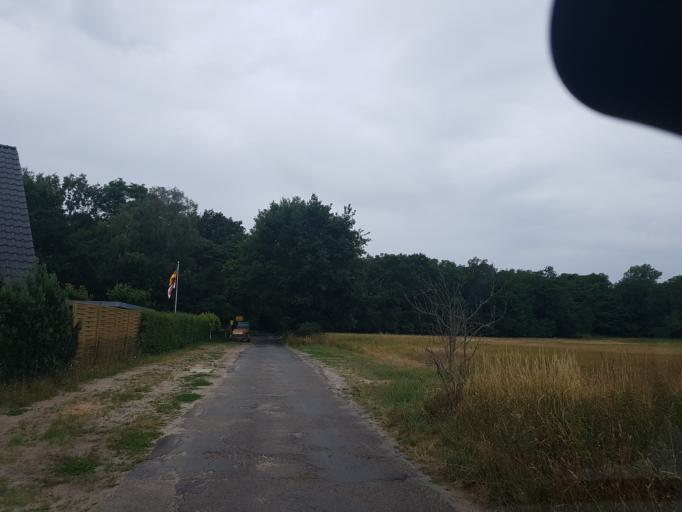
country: DE
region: Brandenburg
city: Teltow
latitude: 52.3731
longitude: 13.2536
